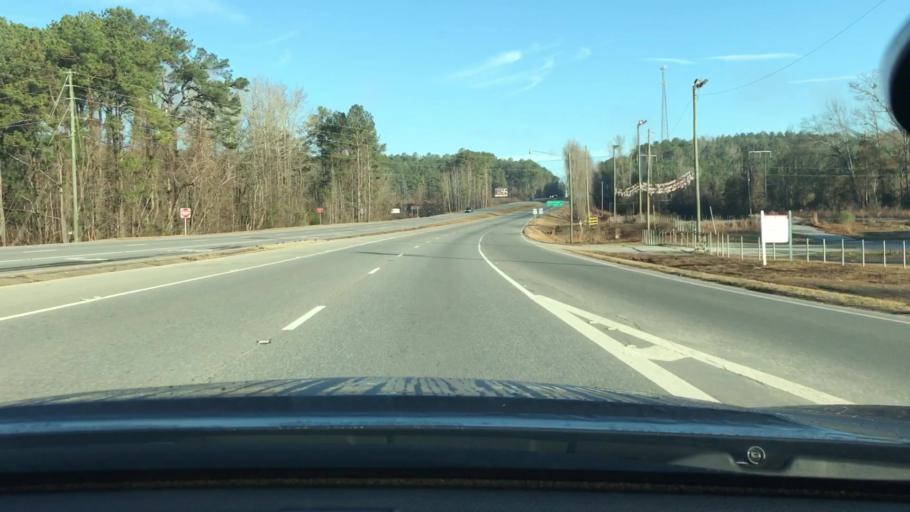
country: US
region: Alabama
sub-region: Talladega County
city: Mignon
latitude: 33.1941
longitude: -86.3078
